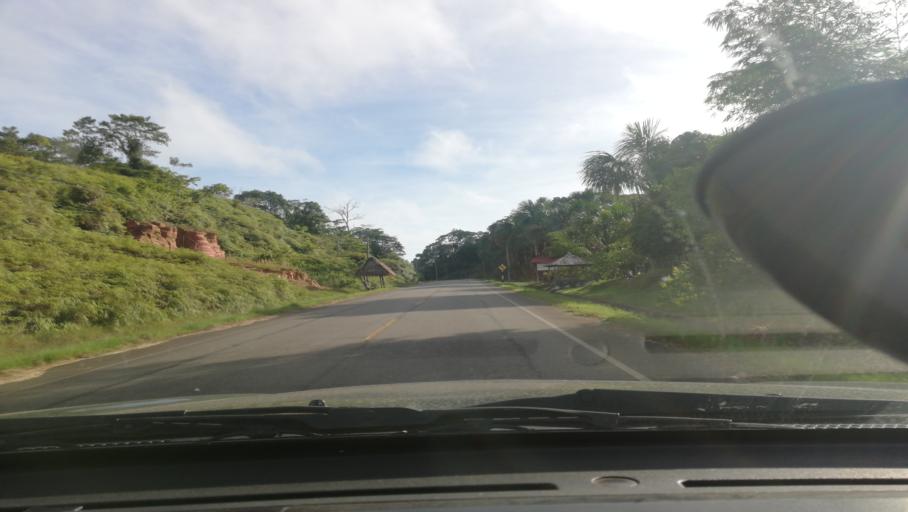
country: PE
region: Loreto
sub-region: Provincia de Loreto
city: Nauta
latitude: -4.4184
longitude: -73.5846
